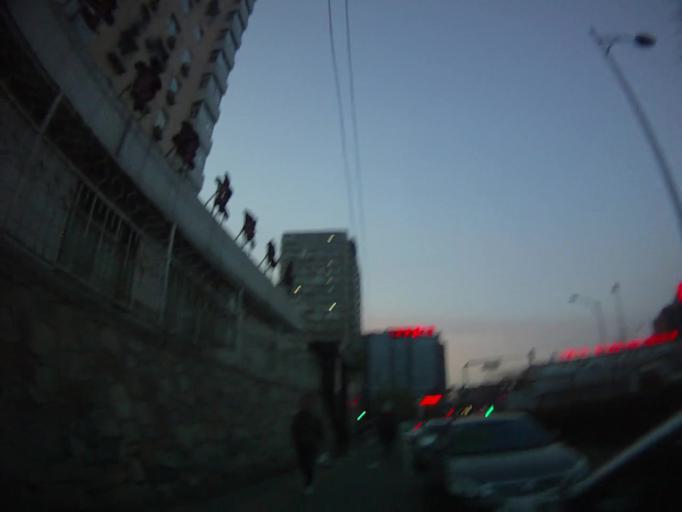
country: CN
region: Beijing
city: Longtan
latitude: 39.8917
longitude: 116.4326
